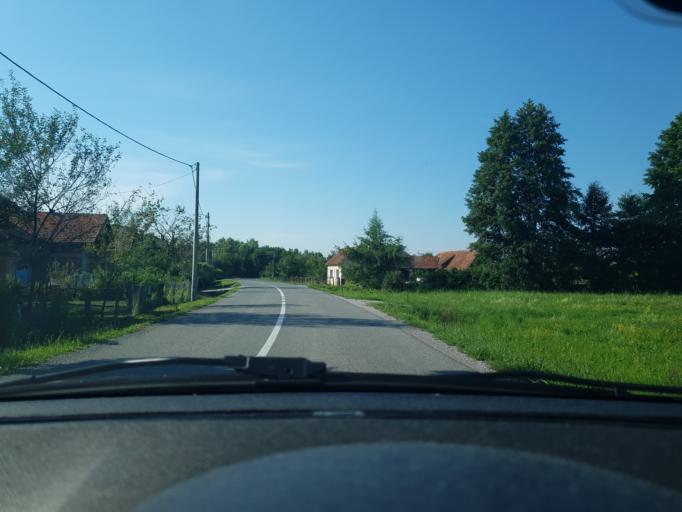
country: HR
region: Zagrebacka
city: Jakovlje
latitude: 45.9255
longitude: 15.8431
